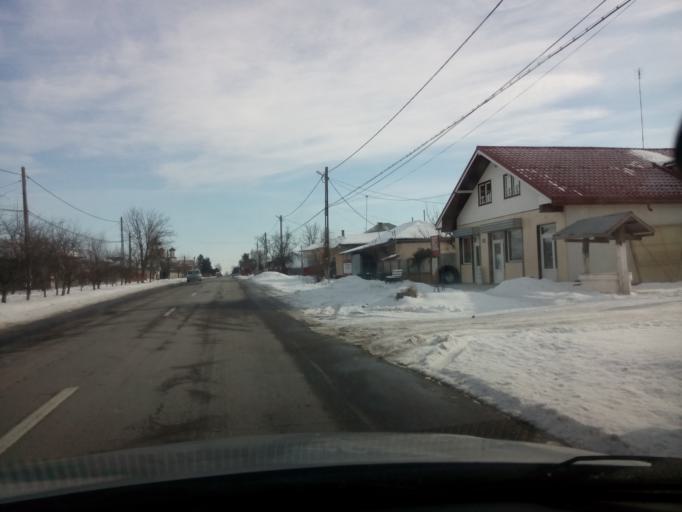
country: RO
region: Calarasi
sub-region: Comuna Soldanu
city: Soldanu
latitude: 44.2233
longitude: 26.5194
